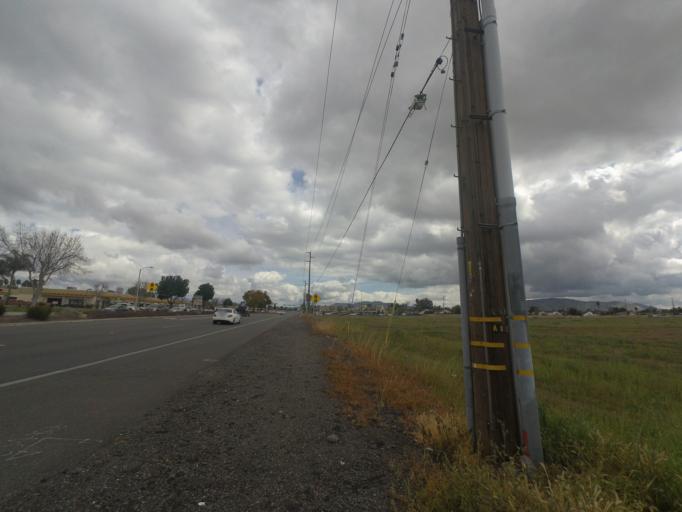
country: US
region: California
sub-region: Riverside County
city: Moreno Valley
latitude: 33.9171
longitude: -117.2463
